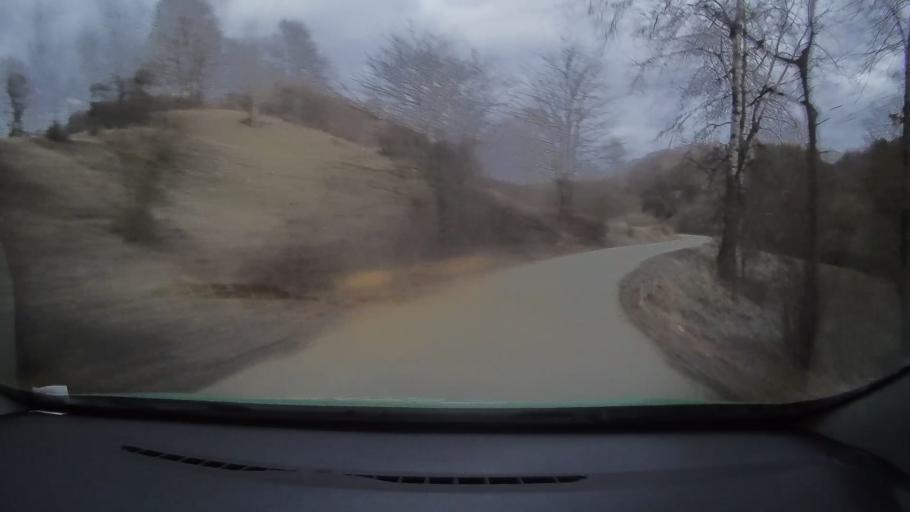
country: RO
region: Prahova
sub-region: Comuna Adunati
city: Adunati
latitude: 45.1233
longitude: 25.6027
